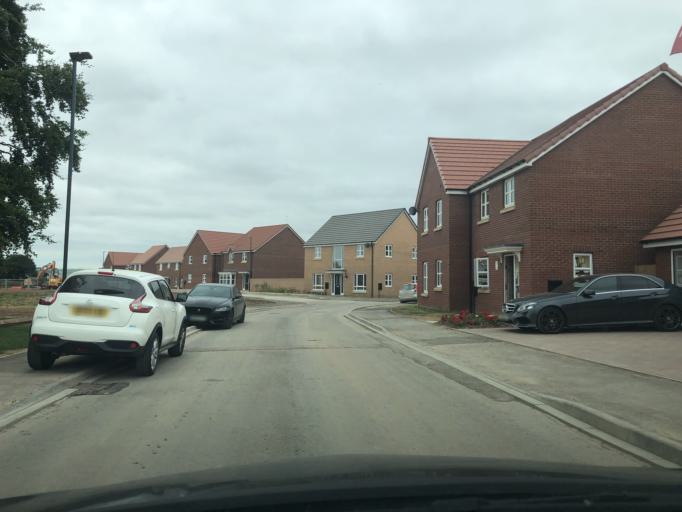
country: GB
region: England
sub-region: North Yorkshire
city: East Ayton
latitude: 54.2432
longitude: -0.4885
